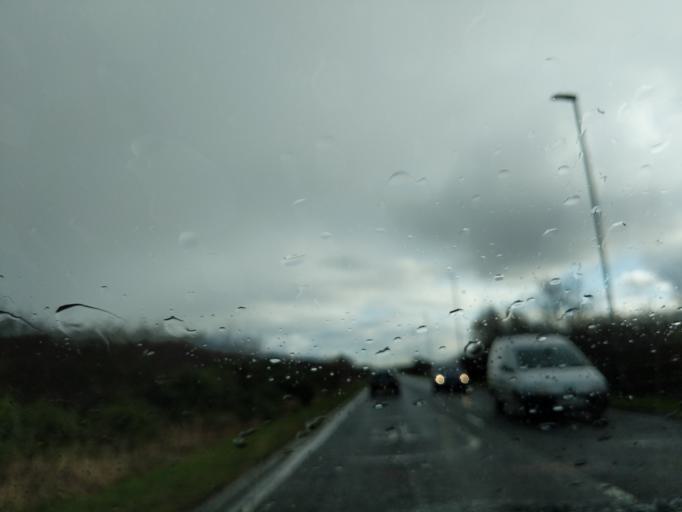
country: GB
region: England
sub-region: Northumberland
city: Seaton Delaval
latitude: 55.1030
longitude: -1.5362
